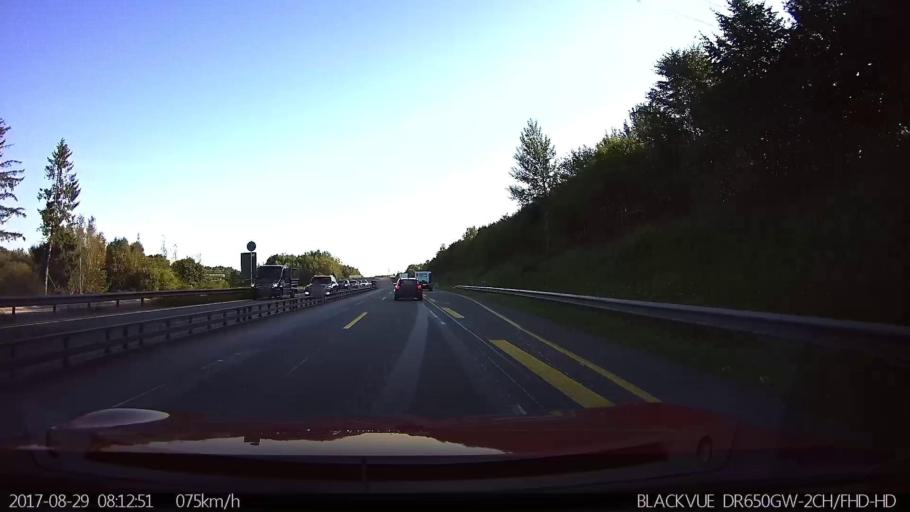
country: DE
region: Schleswig-Holstein
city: Ellerau
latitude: 53.7390
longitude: 9.9459
